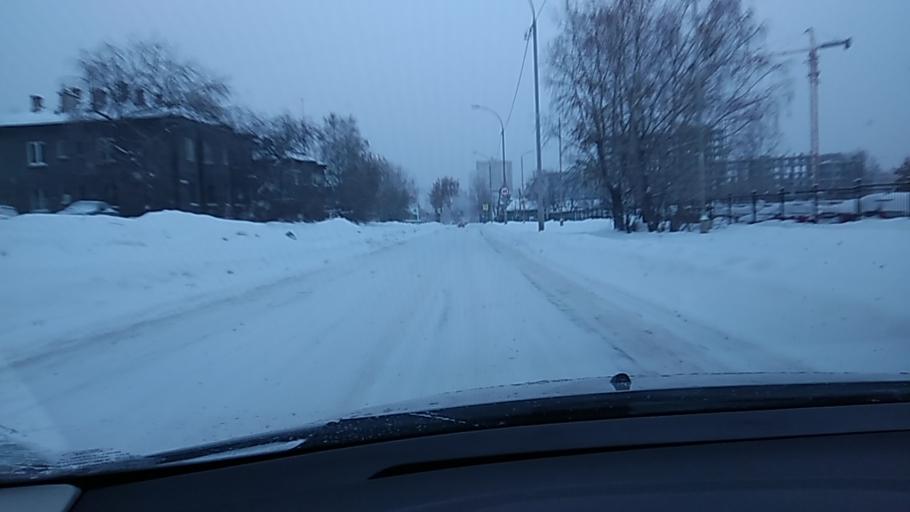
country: RU
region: Sverdlovsk
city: Sovkhoznyy
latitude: 56.8227
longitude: 60.5494
